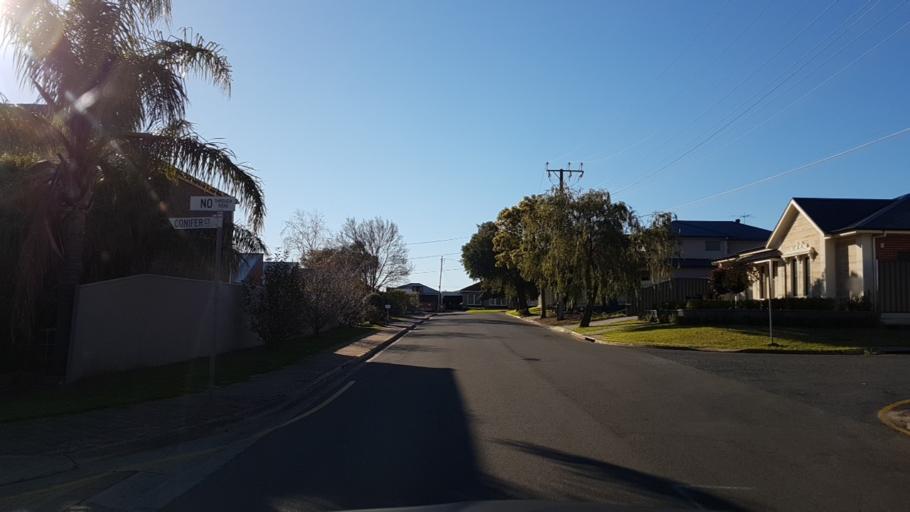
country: AU
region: South Australia
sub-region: Campbelltown
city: Paradise
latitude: -34.8800
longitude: 138.6814
